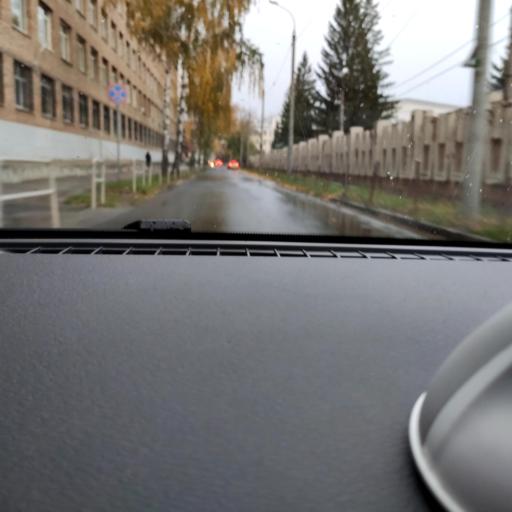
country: RU
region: Samara
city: Samara
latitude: 53.2015
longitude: 50.1055
